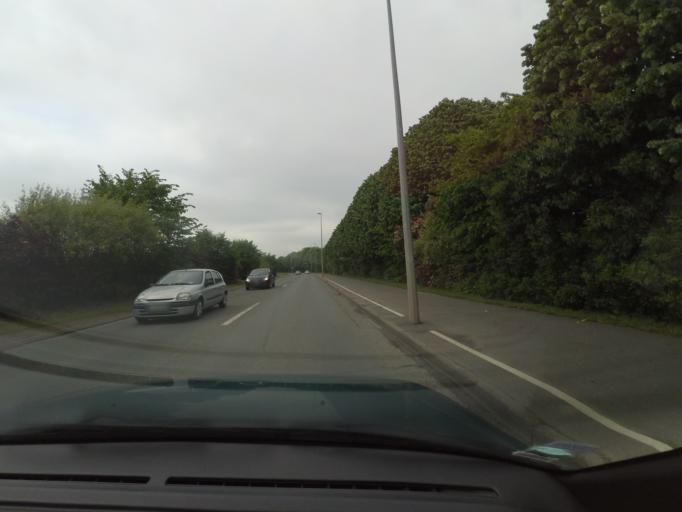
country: FR
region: Pays de la Loire
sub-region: Departement de la Vendee
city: La Roche-sur-Yon
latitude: 46.6839
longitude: -1.4348
